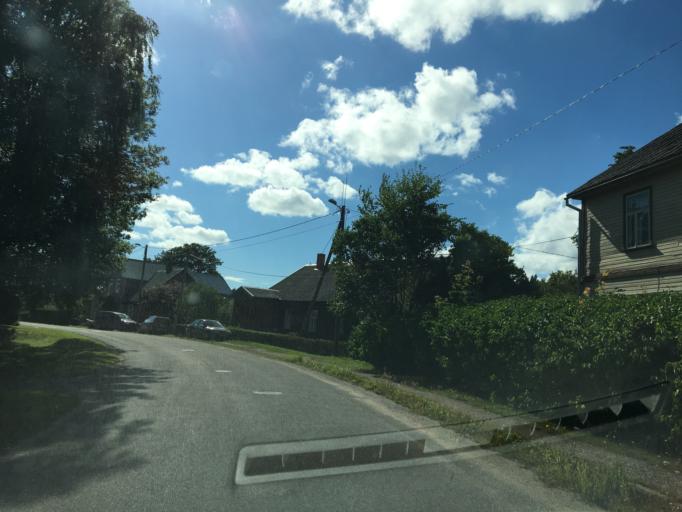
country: EE
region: Paernumaa
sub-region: Vaendra vald (alev)
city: Vandra
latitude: 58.6553
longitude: 25.0480
